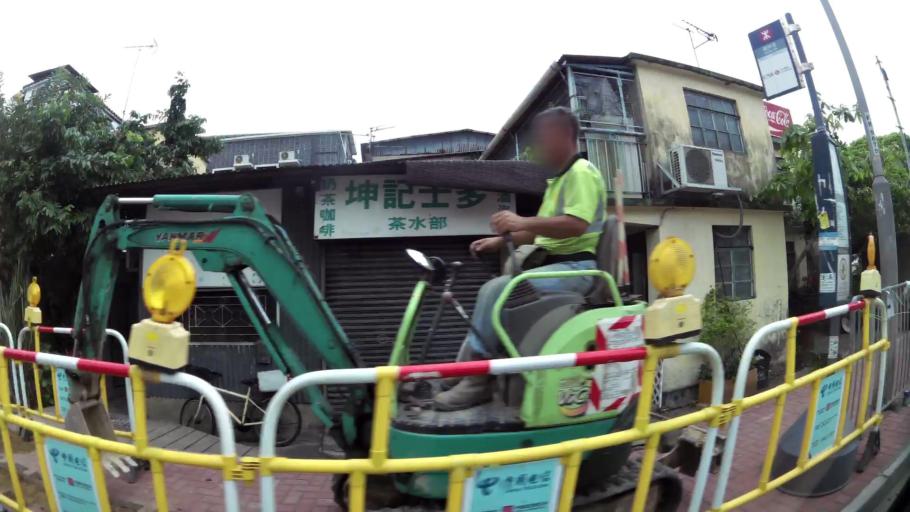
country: HK
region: Yuen Long
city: Yuen Long Kau Hui
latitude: 22.4467
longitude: 113.9938
